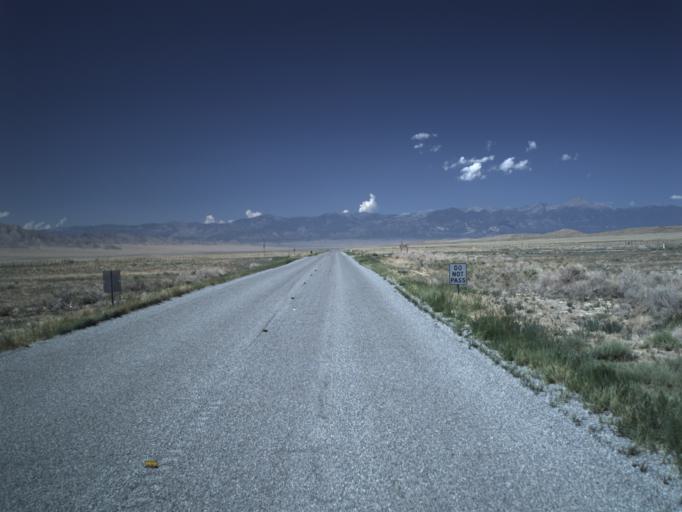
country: US
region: Utah
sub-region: Beaver County
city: Milford
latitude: 39.0606
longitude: -113.7557
